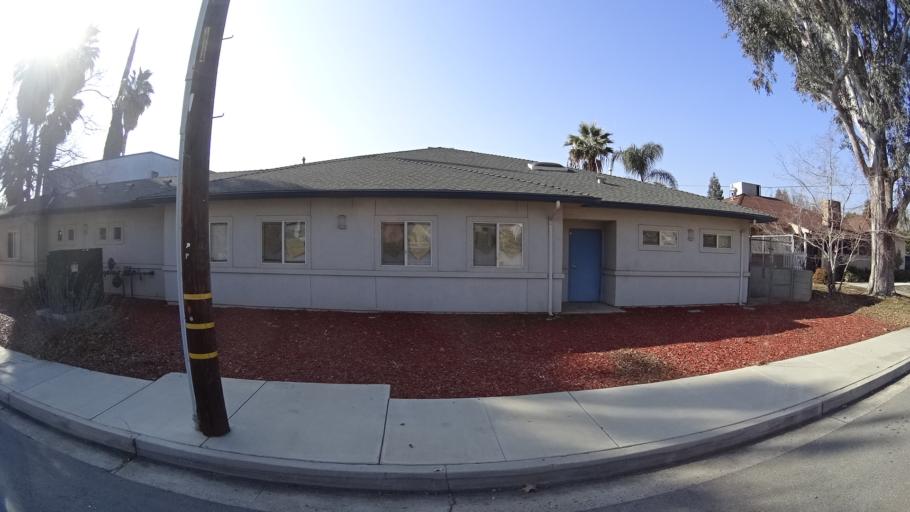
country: US
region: California
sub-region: Kern County
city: Oildale
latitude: 35.4017
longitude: -118.9986
